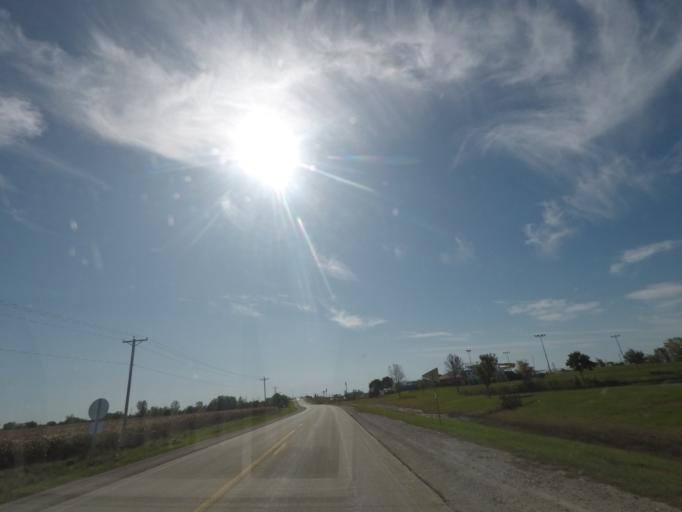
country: US
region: Iowa
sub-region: Story County
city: Nevada
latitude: 42.0145
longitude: -93.4348
